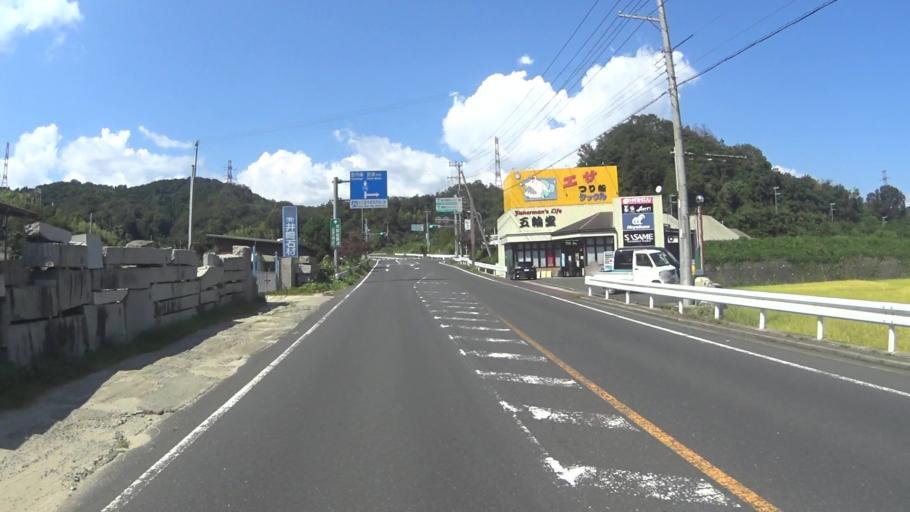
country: JP
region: Kyoto
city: Miyazu
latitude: 35.5506
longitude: 135.2290
